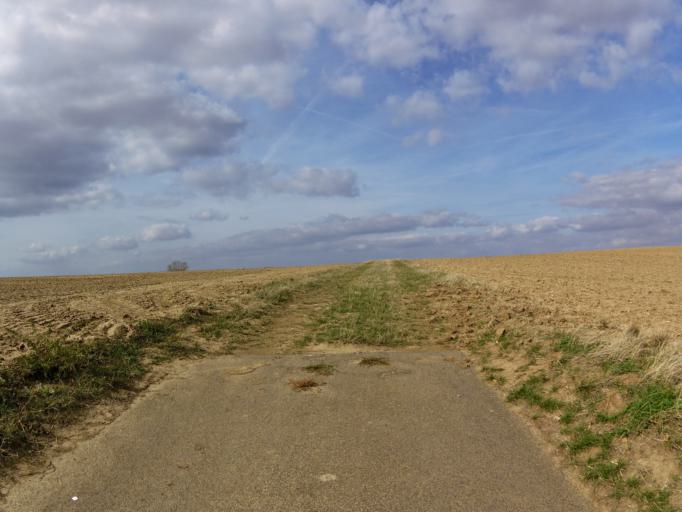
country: DE
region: Bavaria
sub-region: Regierungsbezirk Unterfranken
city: Giebelstadt
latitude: 49.6963
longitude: 9.9564
